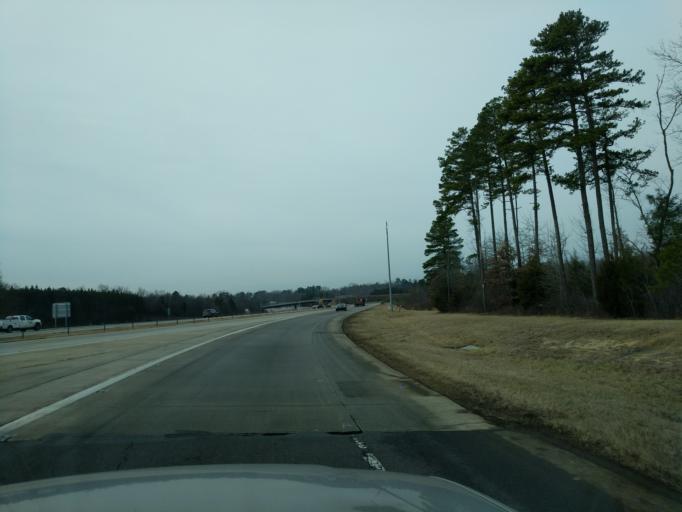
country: US
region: North Carolina
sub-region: Mecklenburg County
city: Huntersville
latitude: 35.3637
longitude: -80.8469
